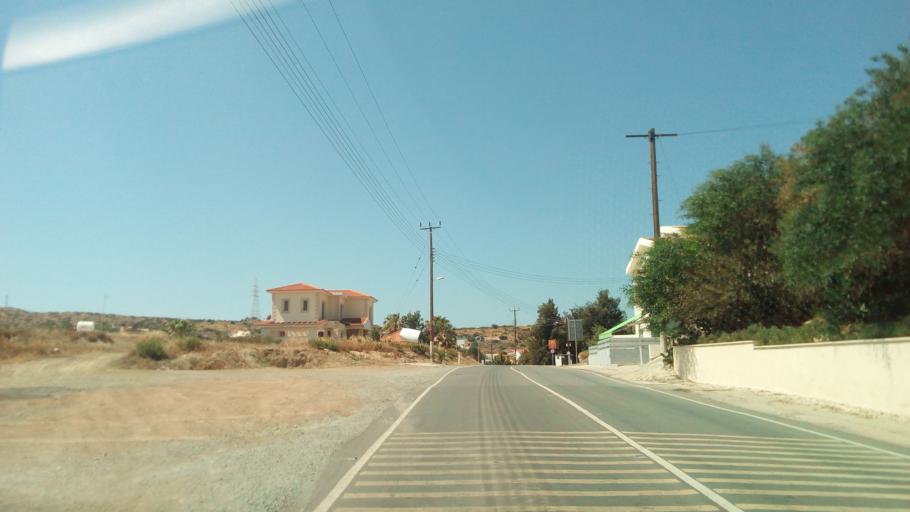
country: CY
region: Limassol
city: Pyrgos
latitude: 34.7354
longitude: 33.1777
